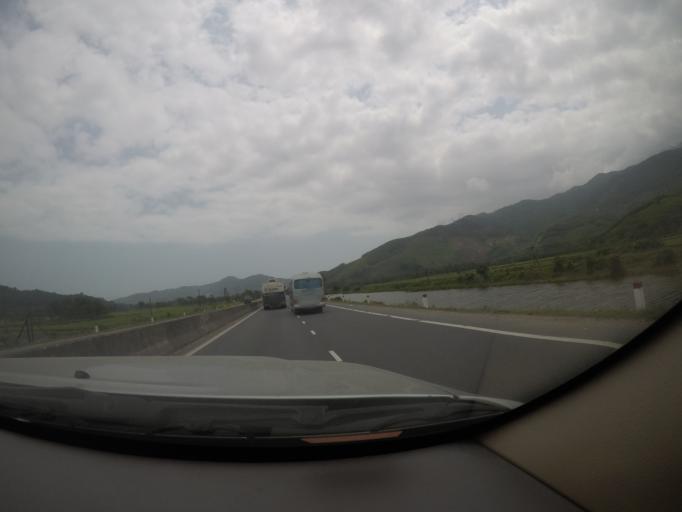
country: VN
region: Thua Thien-Hue
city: Phu Loc
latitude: 16.2710
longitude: 108.0013
